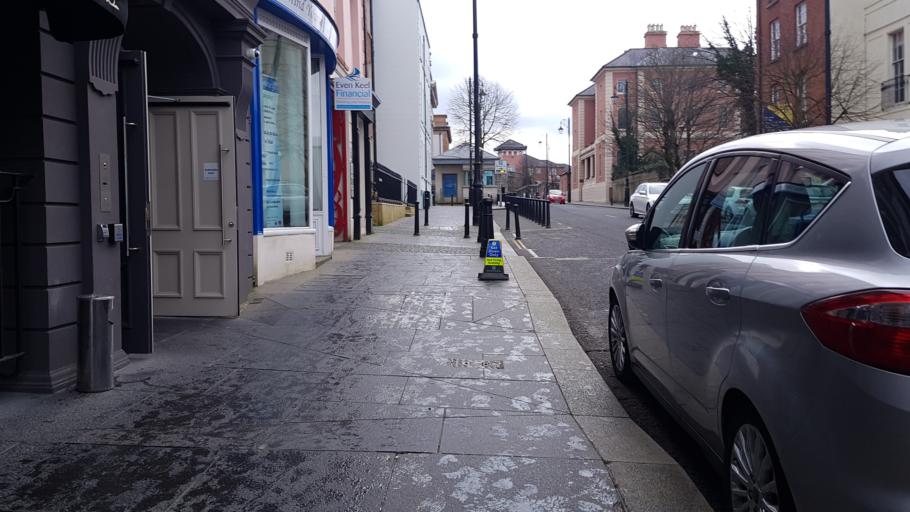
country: GB
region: Northern Ireland
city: Londonderry County Borough
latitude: 54.9948
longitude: -7.3230
